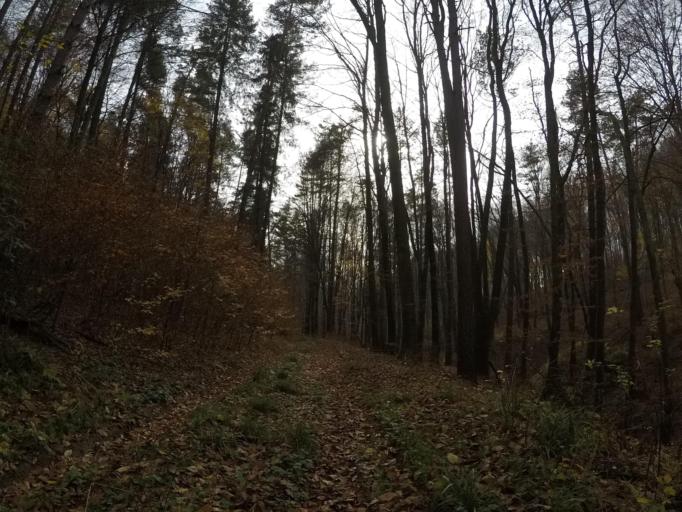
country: SK
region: Presovsky
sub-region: Okres Presov
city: Presov
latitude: 48.9507
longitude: 21.1830
